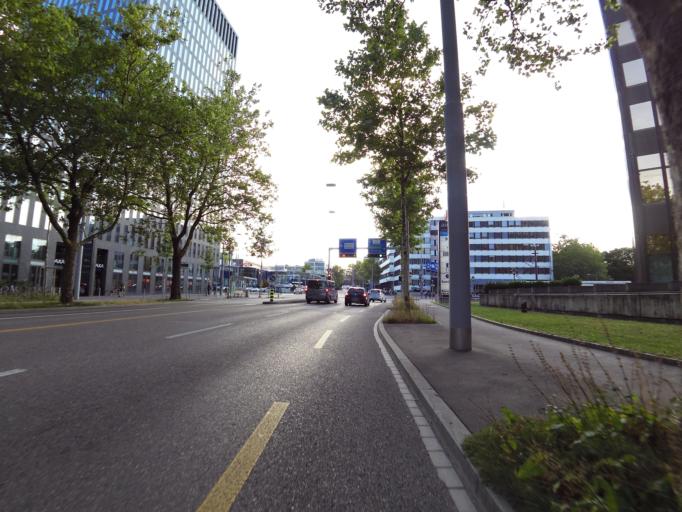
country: CH
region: Zurich
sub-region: Bezirk Zuerich
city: Zuerich (Kreis 11) / Seebach
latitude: 47.4144
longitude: 8.5521
